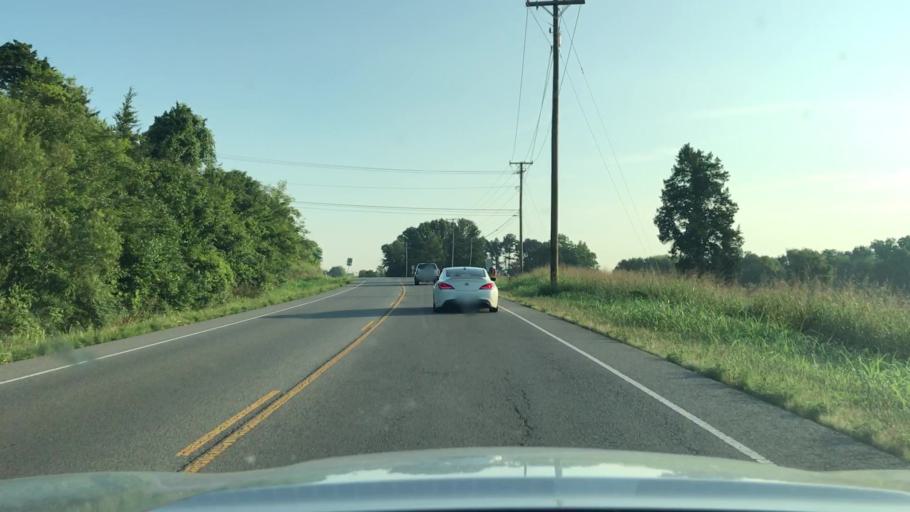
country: US
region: Tennessee
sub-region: Rutherford County
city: La Vergne
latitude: 36.0040
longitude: -86.6219
